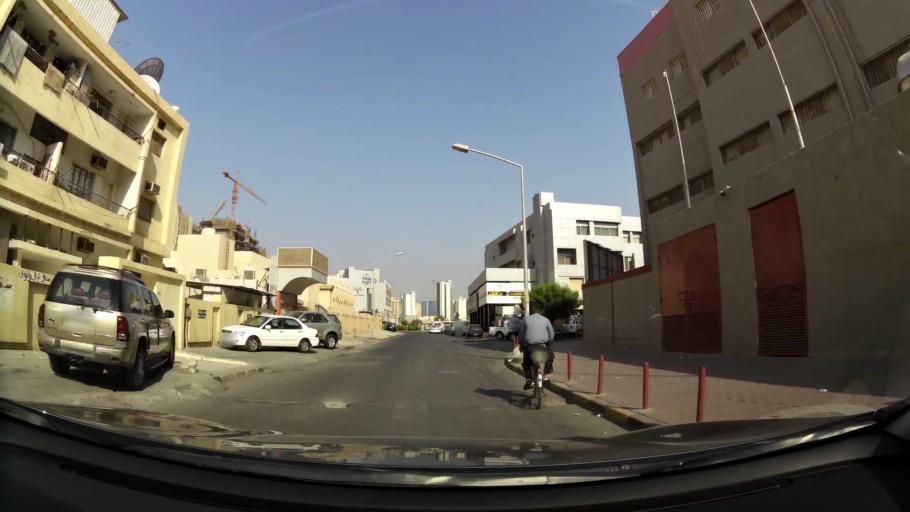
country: KW
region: Muhafazat Hawalli
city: Hawalli
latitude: 29.3359
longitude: 48.0219
